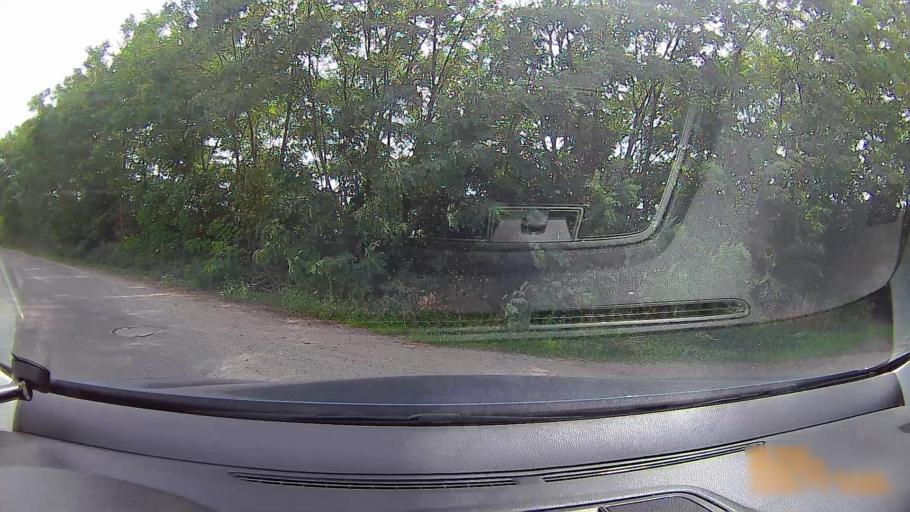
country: PL
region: Greater Poland Voivodeship
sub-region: Powiat koninski
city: Rychwal
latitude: 52.0810
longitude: 18.1557
